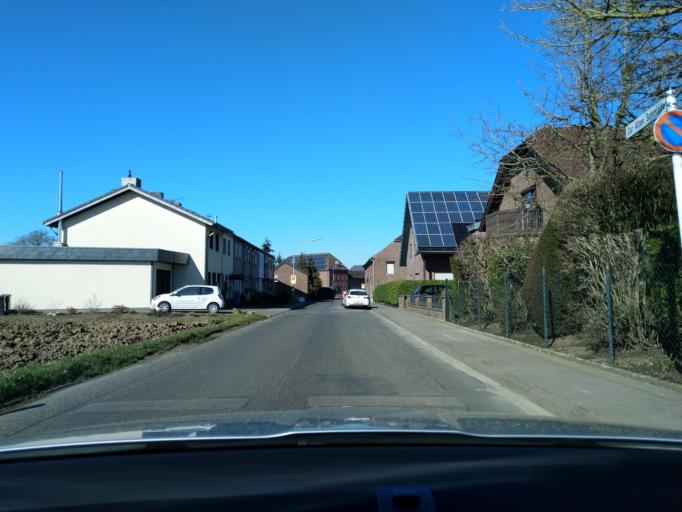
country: DE
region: North Rhine-Westphalia
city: Erkelenz
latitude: 51.1138
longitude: 6.3531
